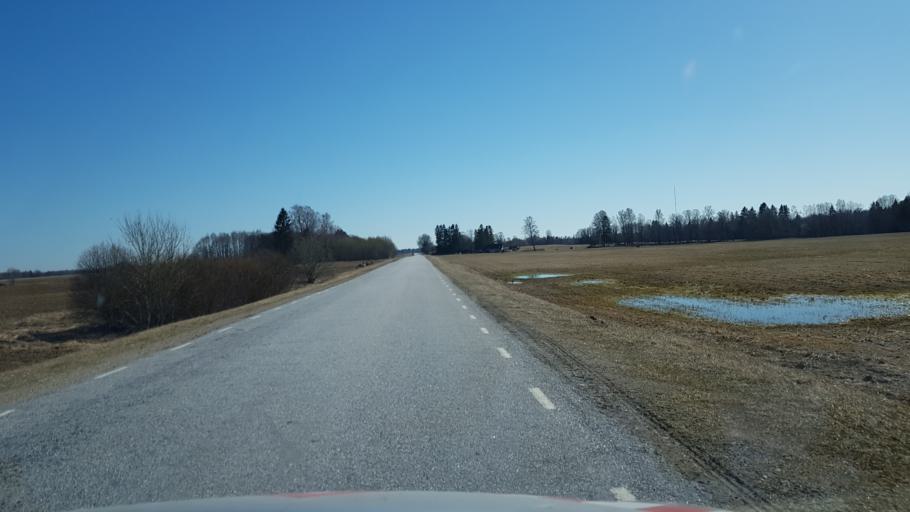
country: EE
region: Jaervamaa
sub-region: Koeru vald
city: Koeru
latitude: 59.0201
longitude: 26.0882
